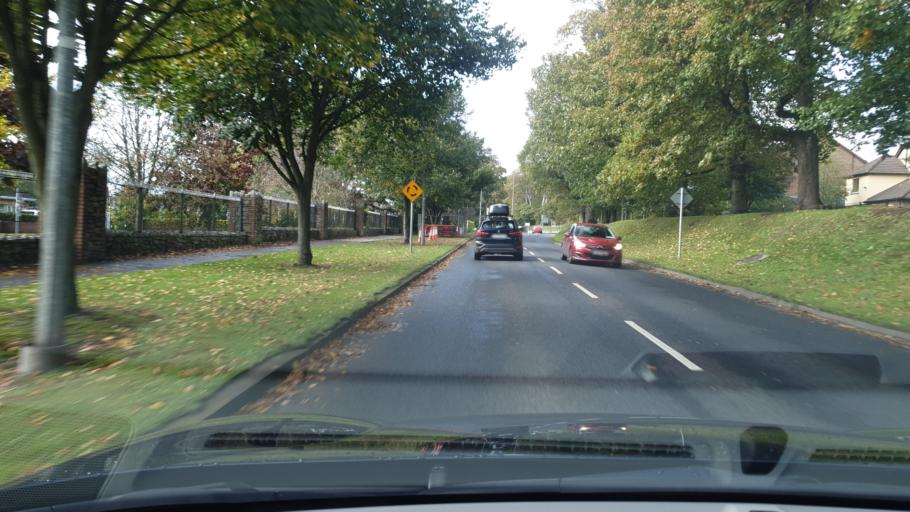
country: IE
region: Leinster
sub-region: An Mhi
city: Ratoath
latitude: 53.5094
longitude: -6.4725
